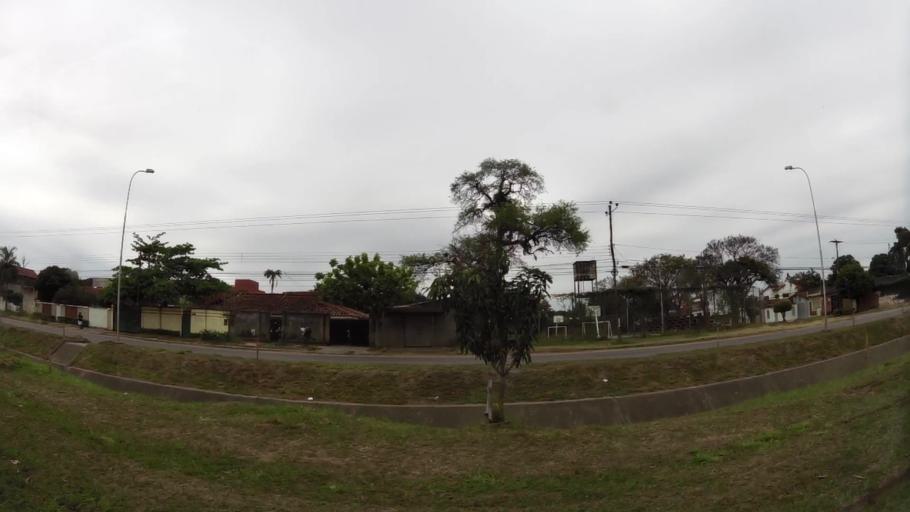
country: BO
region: Santa Cruz
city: Santa Cruz de la Sierra
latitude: -17.8326
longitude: -63.1925
